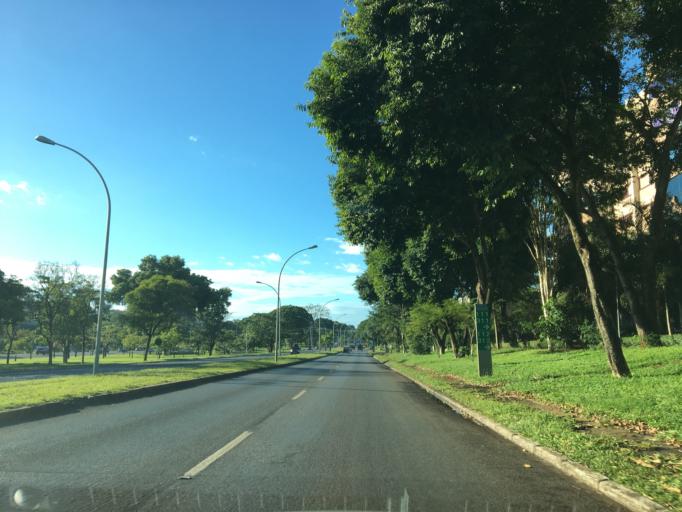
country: BR
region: Federal District
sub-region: Brasilia
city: Brasilia
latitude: -15.7504
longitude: -47.8886
